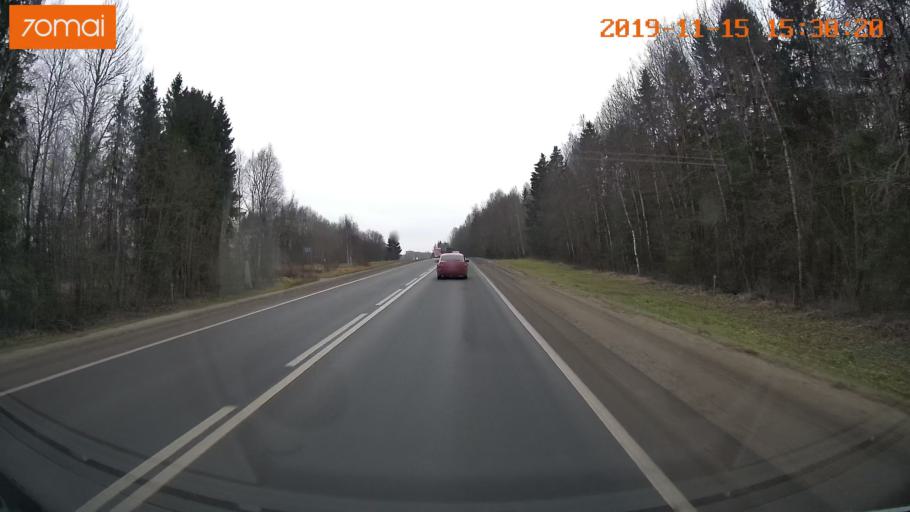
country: RU
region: Jaroslavl
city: Danilov
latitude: 58.1111
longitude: 40.1137
